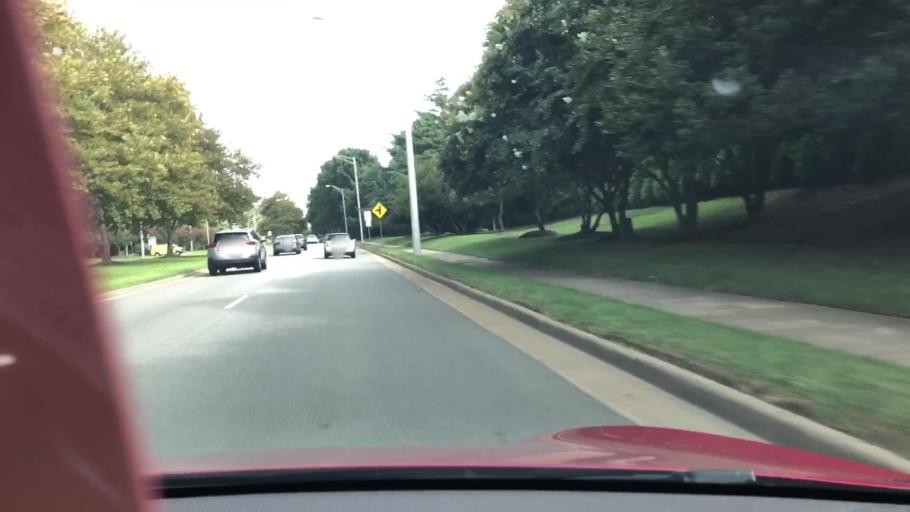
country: US
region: Virginia
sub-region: City of Virginia Beach
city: Virginia Beach
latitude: 36.8947
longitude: -76.0596
